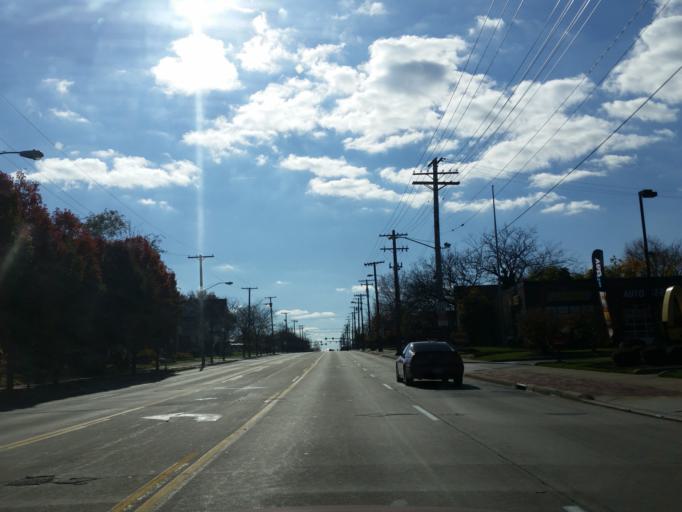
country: US
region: Ohio
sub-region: Cuyahoga County
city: Lakewood
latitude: 41.4828
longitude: -81.7688
